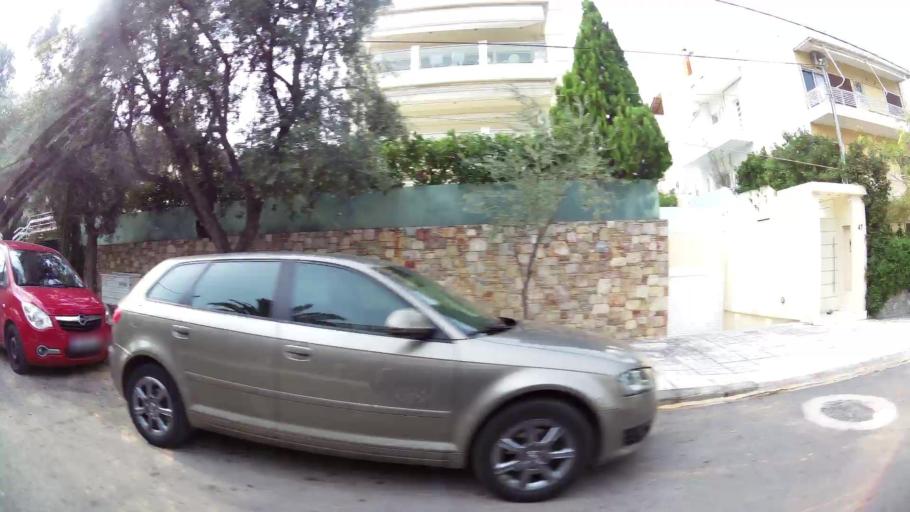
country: GR
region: Attica
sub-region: Nomarchia Athinas
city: Filothei
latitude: 38.0277
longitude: 23.7775
